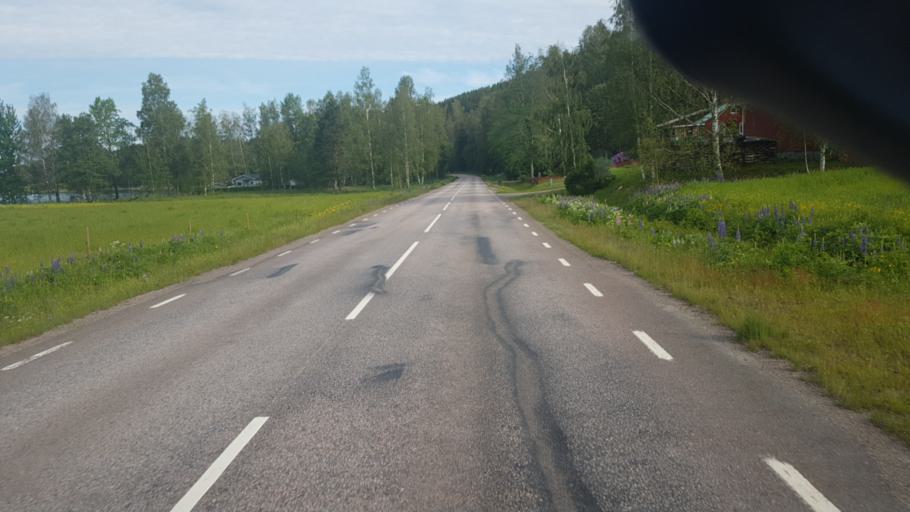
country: SE
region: Vaermland
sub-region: Arvika Kommun
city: Arvika
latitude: 59.7535
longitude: 12.6330
